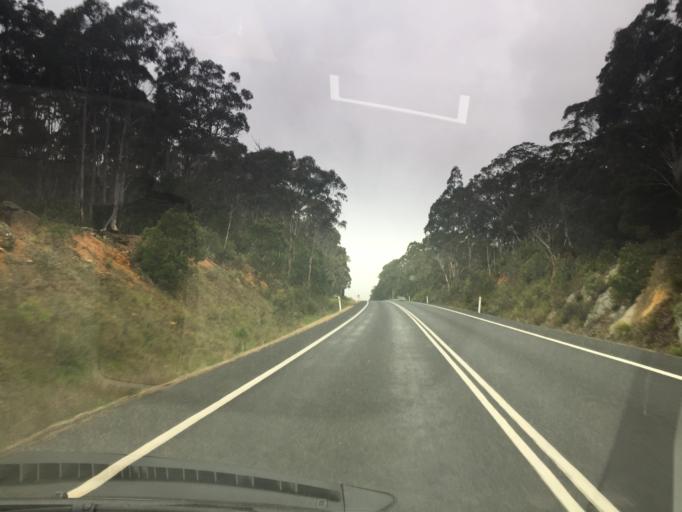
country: AU
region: New South Wales
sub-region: Bombala
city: Bombala
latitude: -36.6138
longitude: 149.3674
